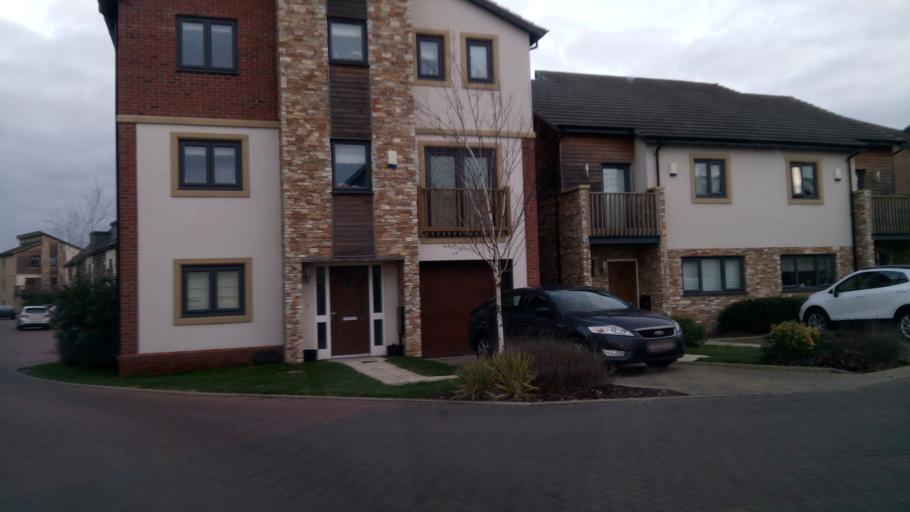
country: GB
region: England
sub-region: Peterborough
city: Peterborough
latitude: 52.5653
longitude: -0.2377
